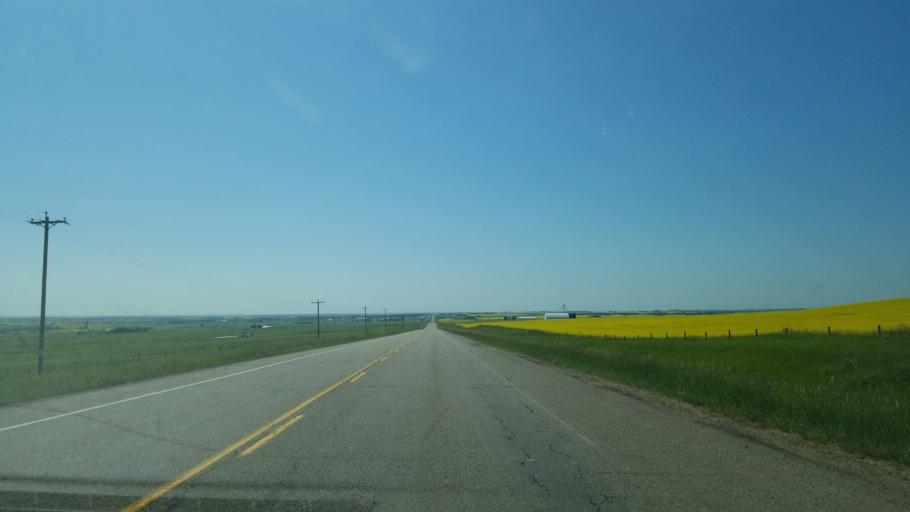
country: CA
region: Alberta
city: Provost
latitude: 52.3612
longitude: -110.1732
